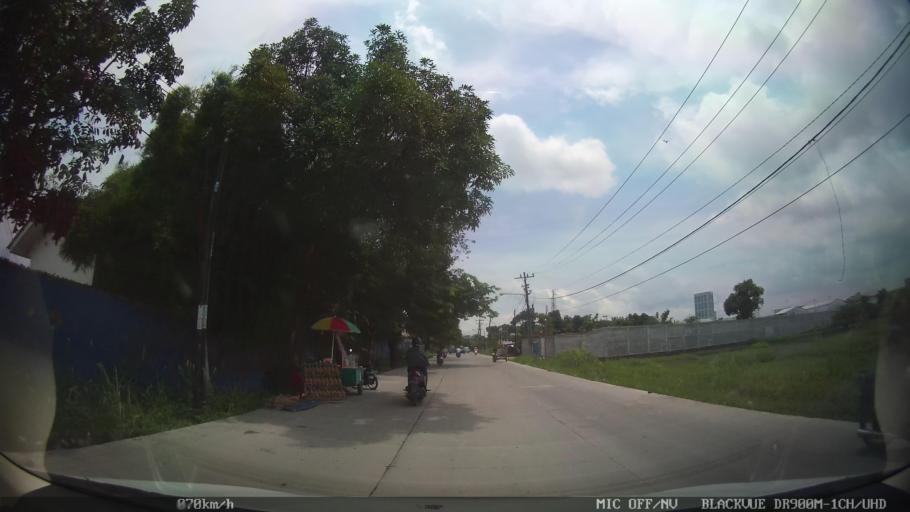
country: ID
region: North Sumatra
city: Labuhan Deli
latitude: 3.6928
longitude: 98.6797
